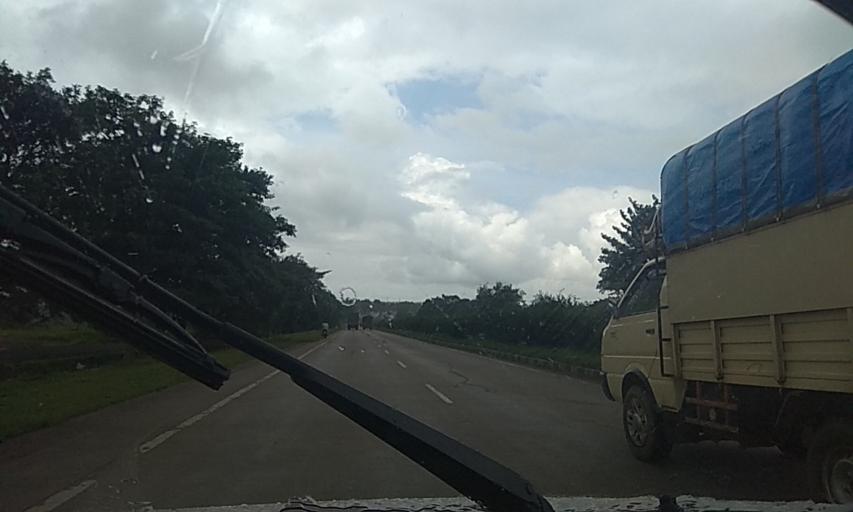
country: IN
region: Karnataka
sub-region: Belgaum
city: Sankeshwar
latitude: 16.2921
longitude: 74.4400
